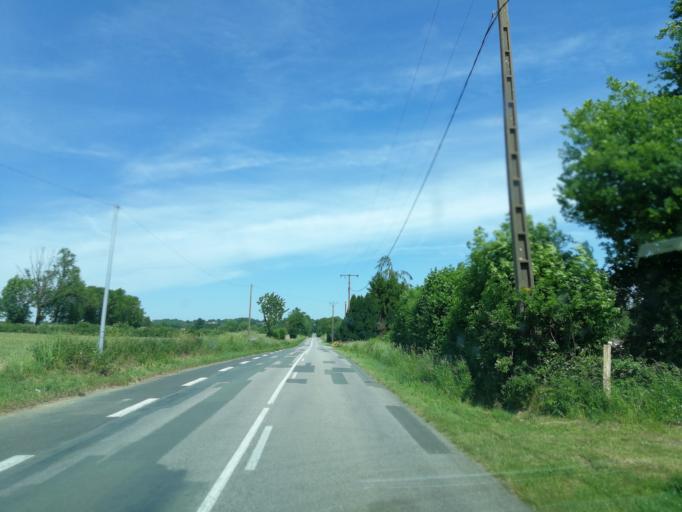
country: FR
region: Poitou-Charentes
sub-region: Departement des Deux-Sevres
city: Courlay
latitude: 46.7915
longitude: -0.6041
